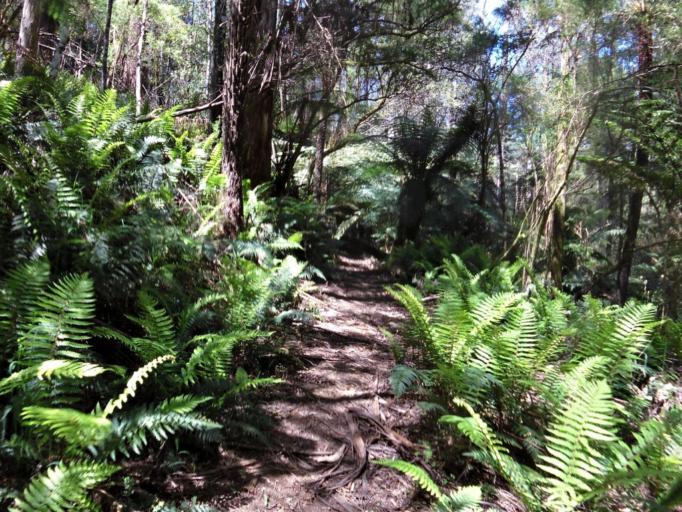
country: AU
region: Victoria
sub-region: Yarra Ranges
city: Millgrove
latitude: -37.8586
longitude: 145.7621
